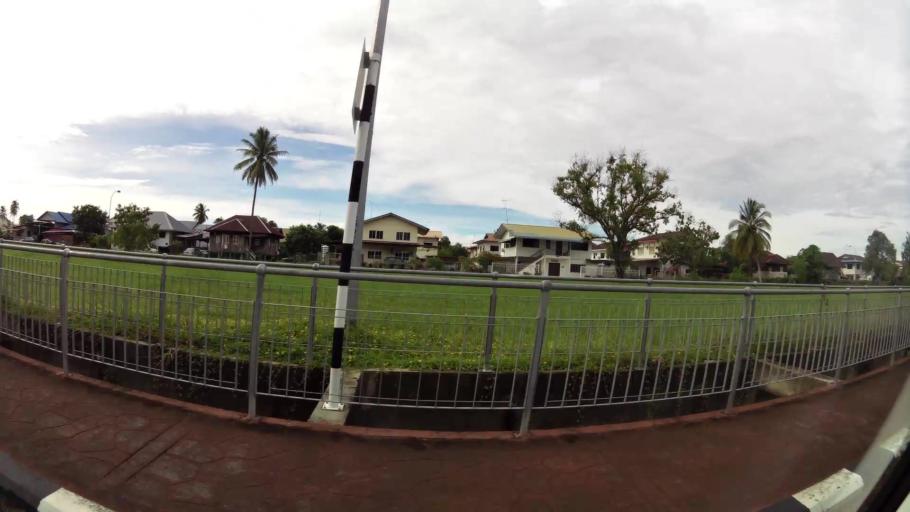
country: BN
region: Belait
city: Seria
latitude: 4.6129
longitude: 114.3337
